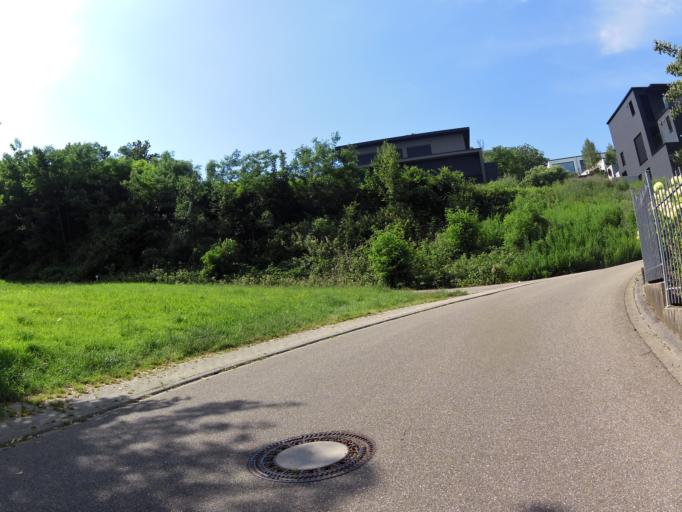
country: DE
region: Baden-Wuerttemberg
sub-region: Freiburg Region
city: Lahr
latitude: 48.3450
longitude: 7.8567
